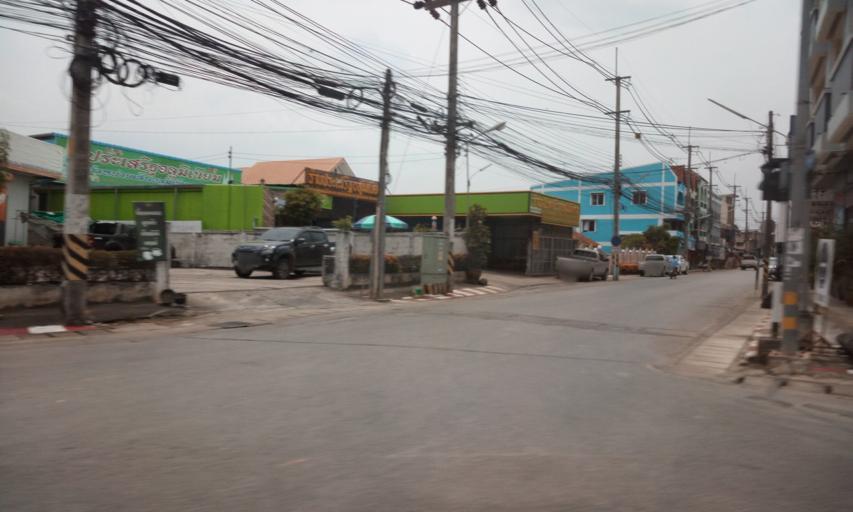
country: TH
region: Phayao
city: Chiang Kham
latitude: 19.5239
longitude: 100.3051
